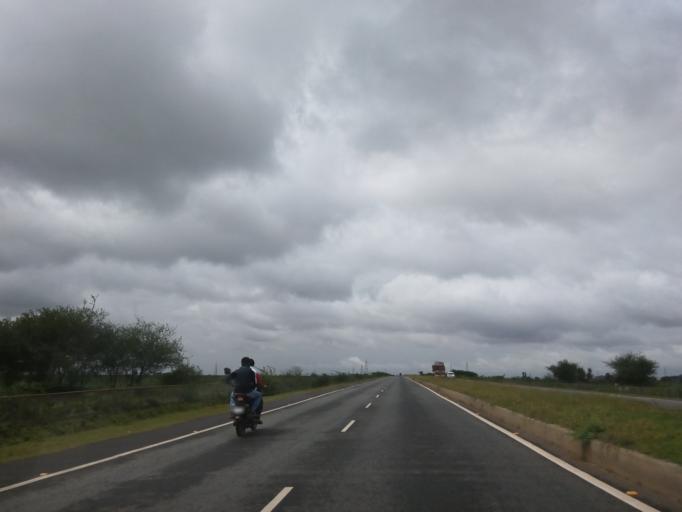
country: IN
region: Karnataka
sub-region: Haveri
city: Haveri
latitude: 14.8024
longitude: 75.3773
